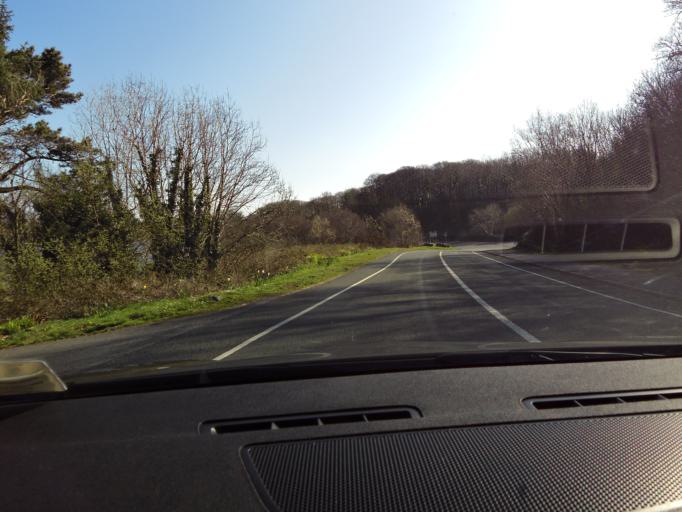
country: IE
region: Connaught
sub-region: County Galway
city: Clifden
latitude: 53.4792
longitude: -10.0199
